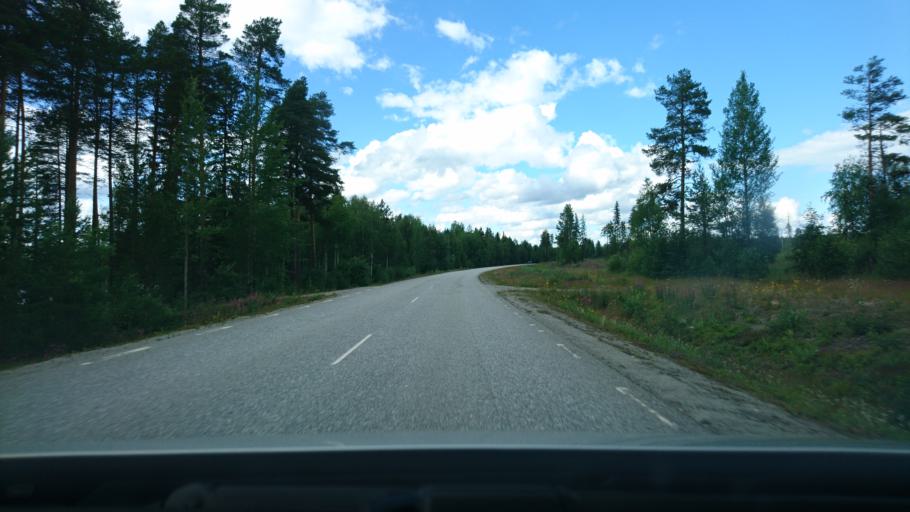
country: SE
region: Vaesterbotten
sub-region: Asele Kommun
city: Asele
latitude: 63.9696
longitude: 17.2637
